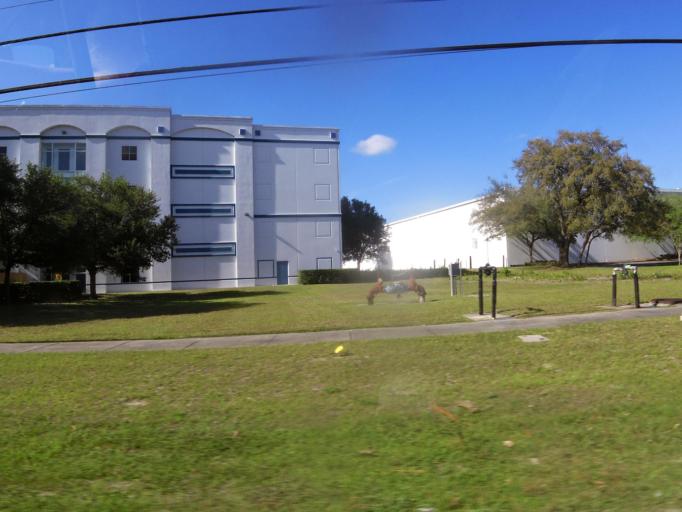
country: US
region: Florida
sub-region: Duval County
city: Jacksonville
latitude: 30.4363
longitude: -81.5751
